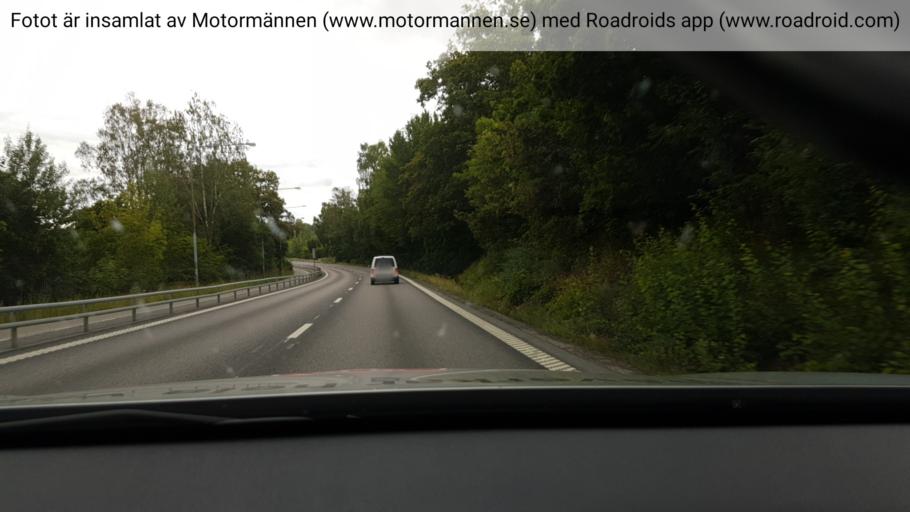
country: SE
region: Stockholm
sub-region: Tyreso Kommun
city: Bollmora
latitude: 59.2188
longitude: 18.2037
